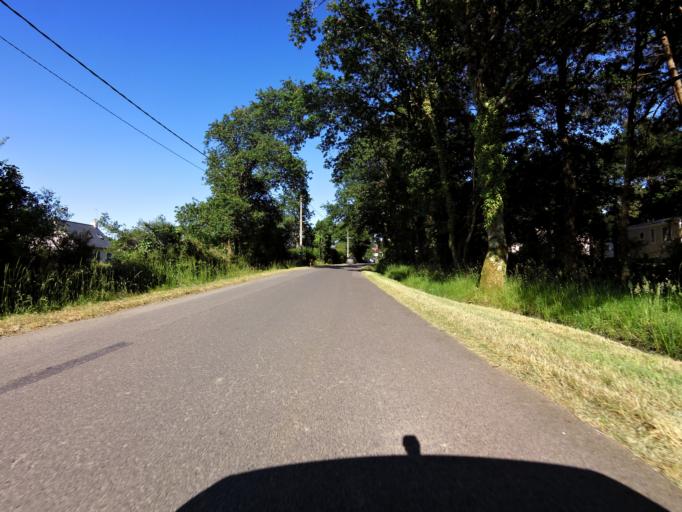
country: FR
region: Brittany
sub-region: Departement du Morbihan
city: Penestin
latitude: 47.4732
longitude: -2.4634
